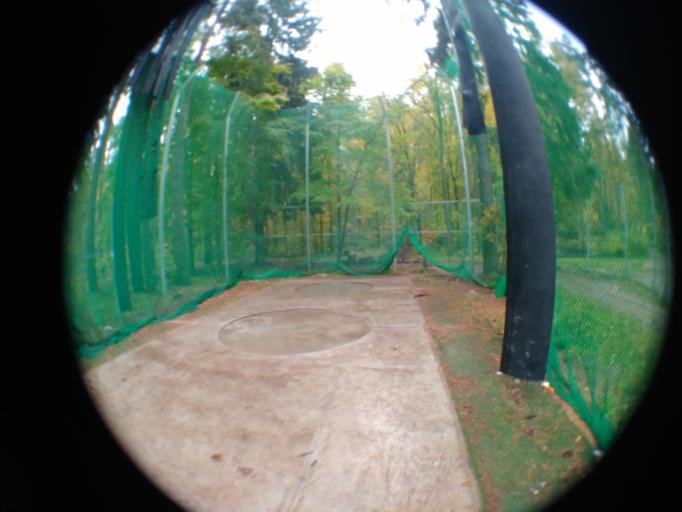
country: RU
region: Moskovskaya
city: Zhukovskiy
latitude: 55.5843
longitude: 38.1270
